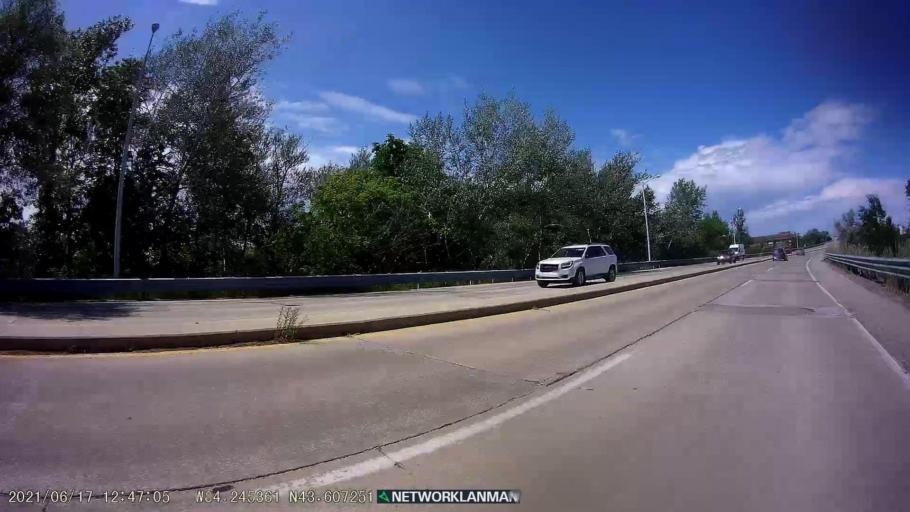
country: US
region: Michigan
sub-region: Midland County
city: Midland
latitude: 43.6075
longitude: -84.2454
